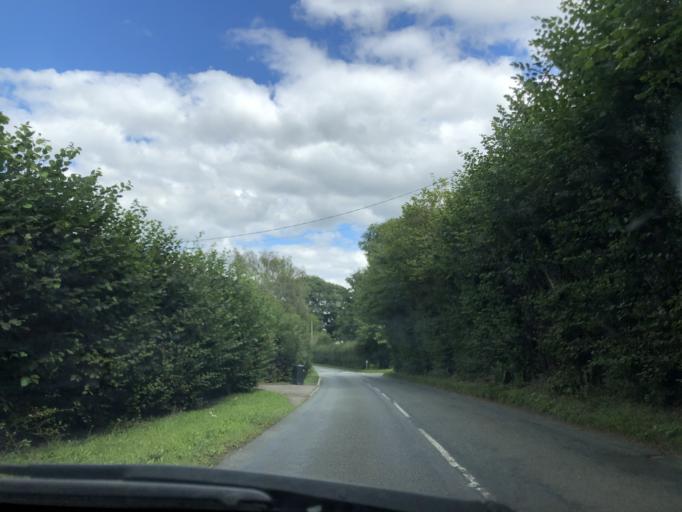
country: GB
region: England
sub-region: East Sussex
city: Forest Row
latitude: 51.0362
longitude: 0.0566
